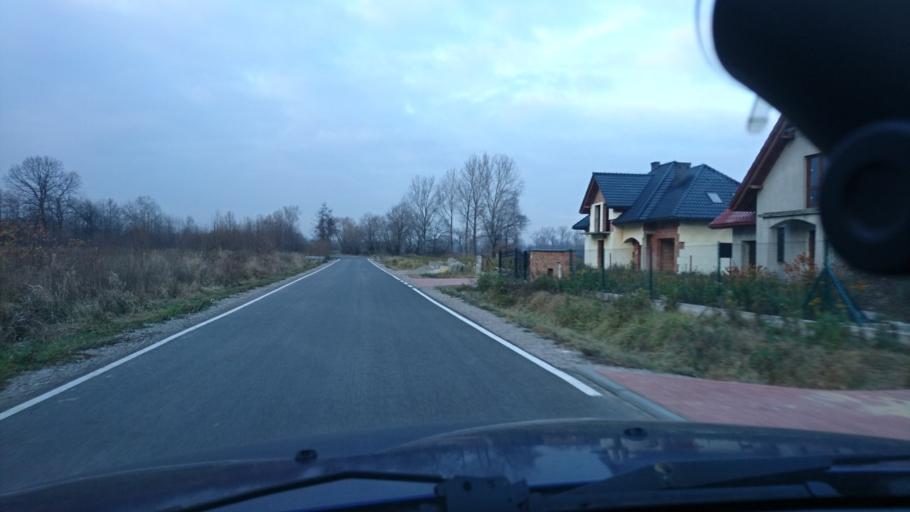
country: PL
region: Silesian Voivodeship
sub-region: Powiat bielski
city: Bestwinka
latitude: 49.9423
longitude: 19.0751
